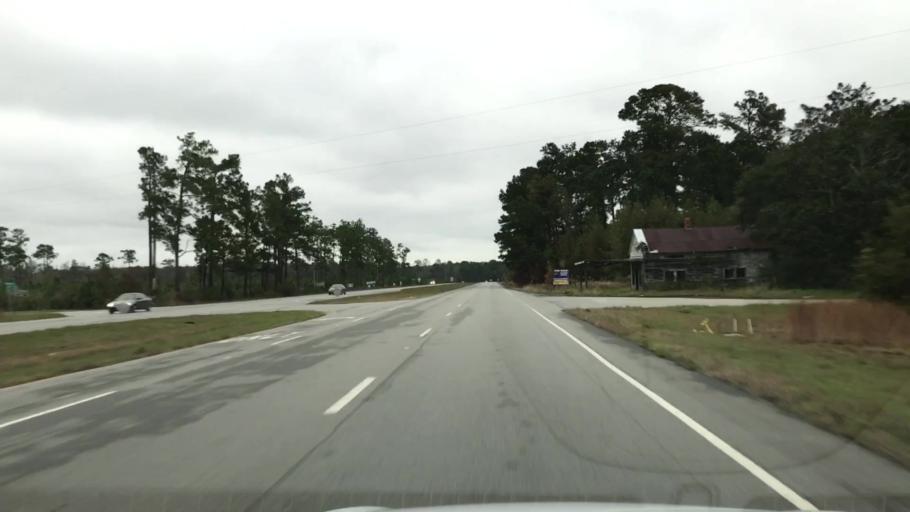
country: US
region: South Carolina
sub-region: Georgetown County
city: Georgetown
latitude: 33.1732
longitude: -79.4175
